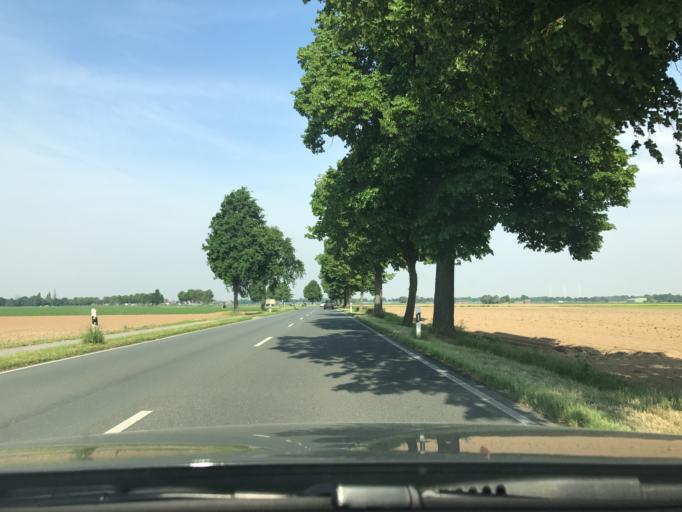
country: DE
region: North Rhine-Westphalia
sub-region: Regierungsbezirk Dusseldorf
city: Rheurdt
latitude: 51.4426
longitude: 6.4458
